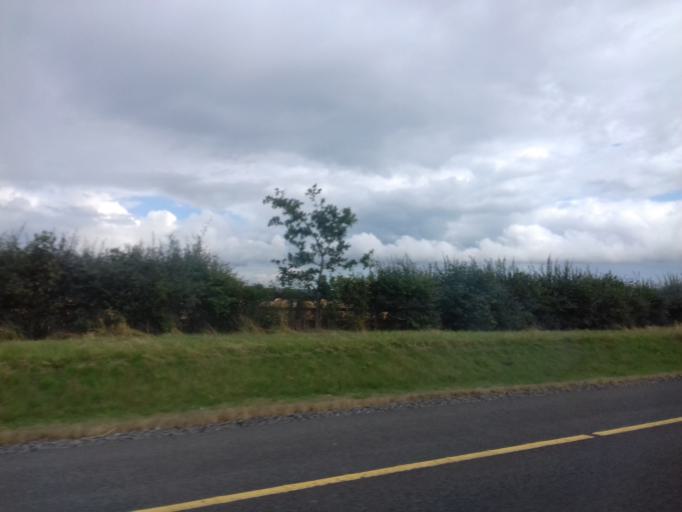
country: IE
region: Leinster
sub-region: Kilkenny
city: Kilkenny
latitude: 52.5493
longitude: -7.2489
